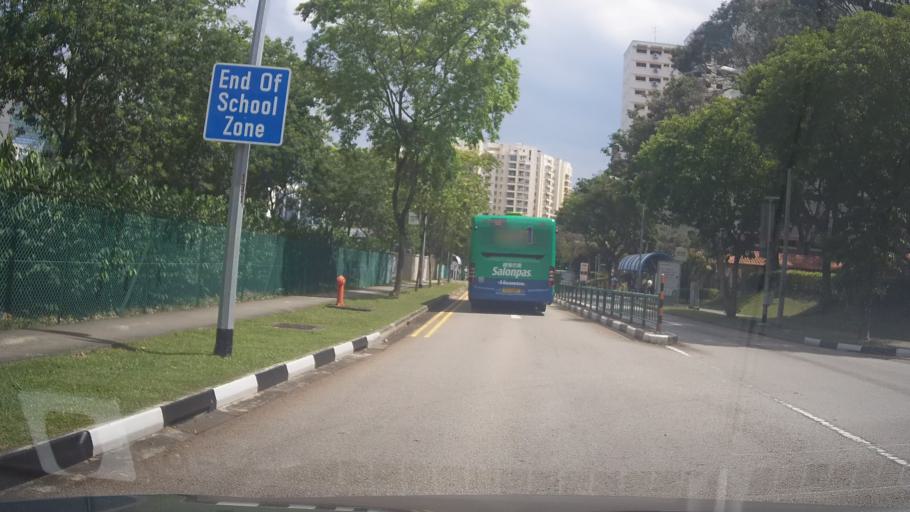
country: MY
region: Johor
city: Kampung Pasir Gudang Baru
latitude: 1.3762
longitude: 103.9365
